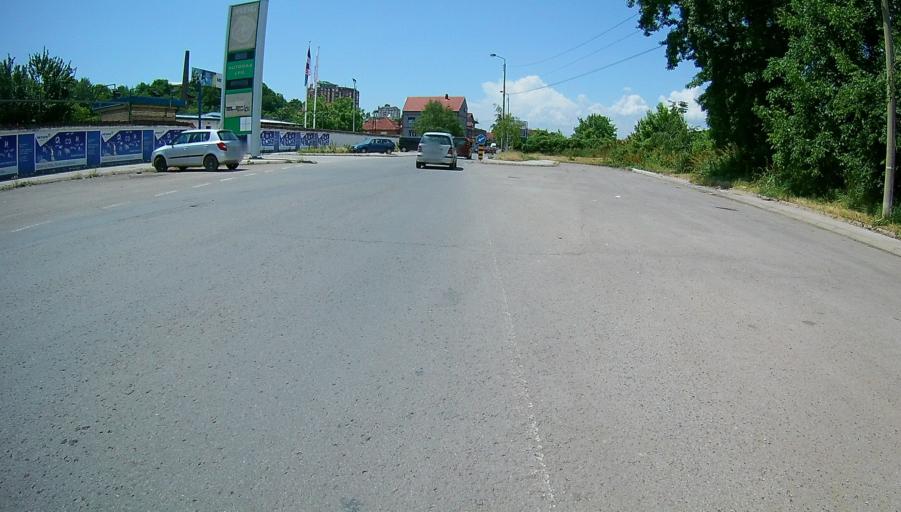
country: RS
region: Central Serbia
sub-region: Nisavski Okrug
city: Nis
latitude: 43.3121
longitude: 21.9071
